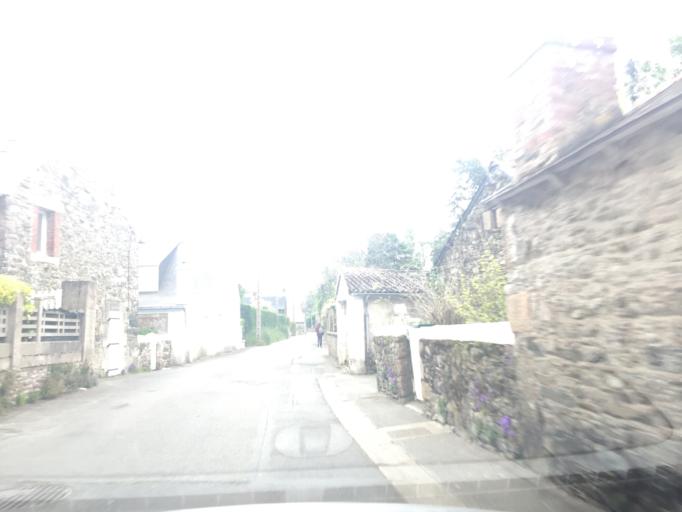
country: FR
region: Brittany
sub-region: Departement des Cotes-d'Armor
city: Paimpol
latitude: 48.7802
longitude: -3.0360
